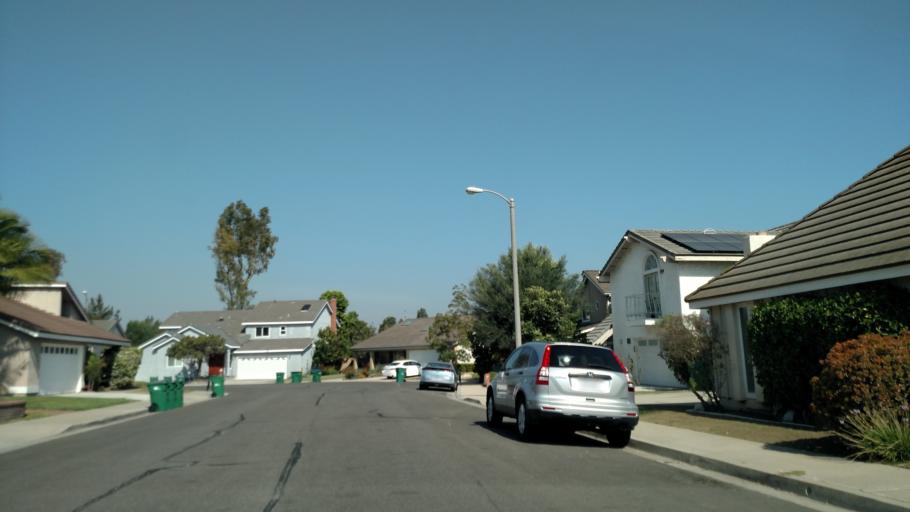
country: US
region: California
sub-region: Orange County
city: Irvine
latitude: 33.6905
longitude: -117.7907
